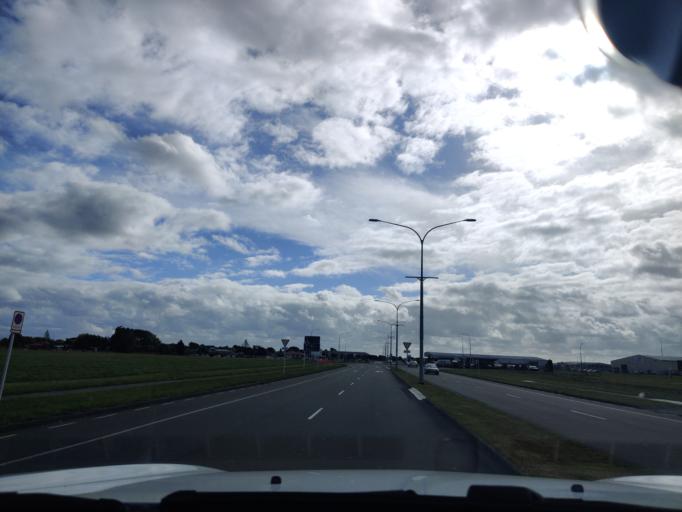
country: NZ
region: Manawatu-Wanganui
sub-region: Palmerston North City
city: Palmerston North
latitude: -40.3255
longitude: 175.6226
